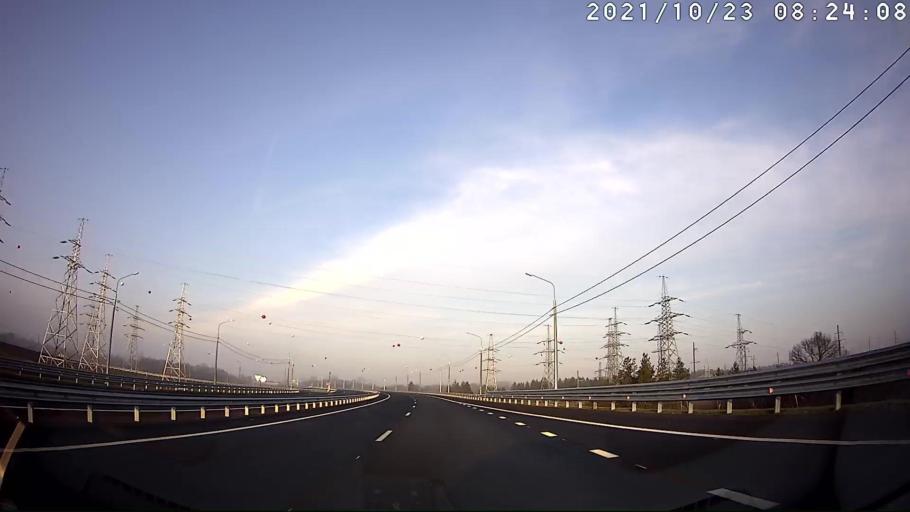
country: RU
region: Saratov
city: Sennoy
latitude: 52.1442
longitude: 46.9115
